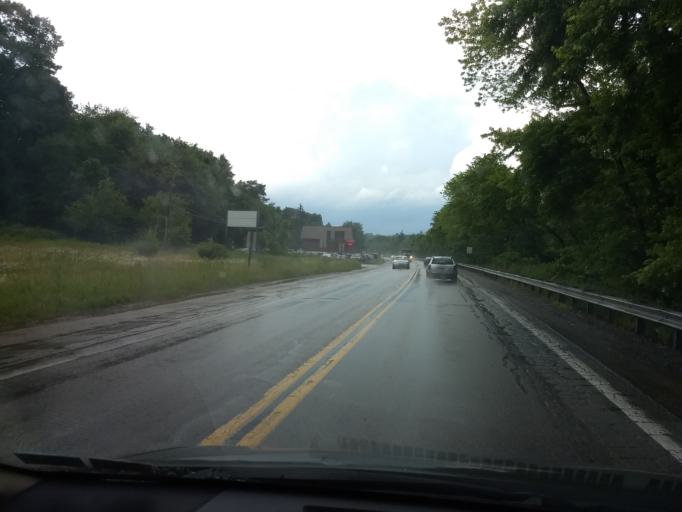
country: US
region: Pennsylvania
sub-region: Westmoreland County
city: Murrysville
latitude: 40.4653
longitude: -79.7053
